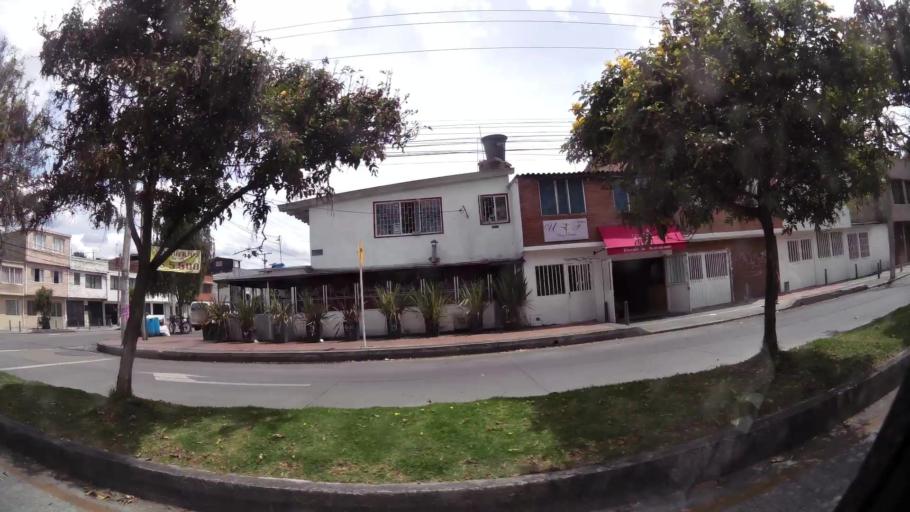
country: CO
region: Cundinamarca
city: Funza
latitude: 4.7099
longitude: -74.1158
